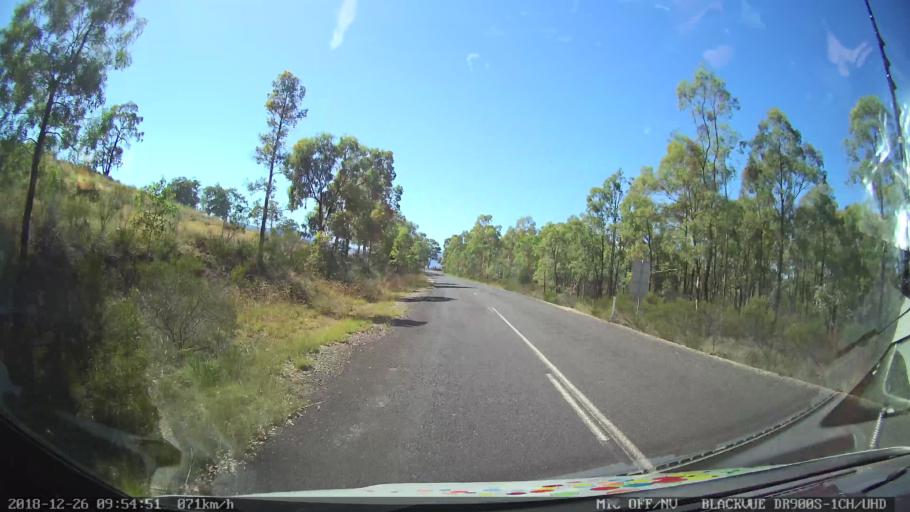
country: AU
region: New South Wales
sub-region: Mid-Western Regional
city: Kandos
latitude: -33.0343
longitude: 150.1619
